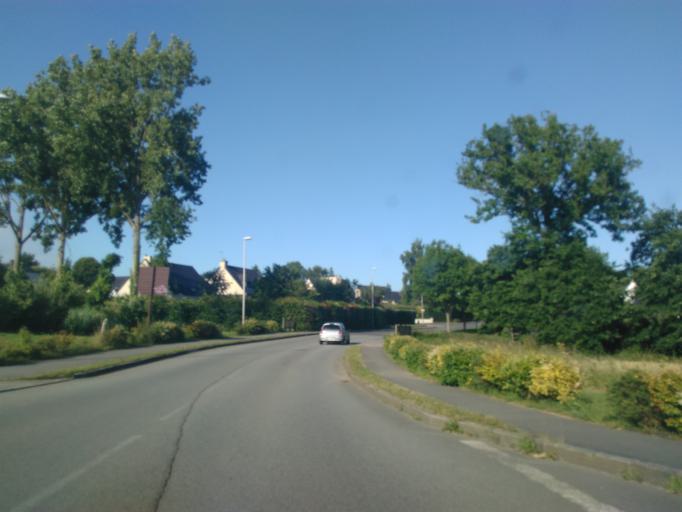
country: FR
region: Brittany
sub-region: Departement d'Ille-et-Vilaine
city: Geveze
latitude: 48.2212
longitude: -1.8012
